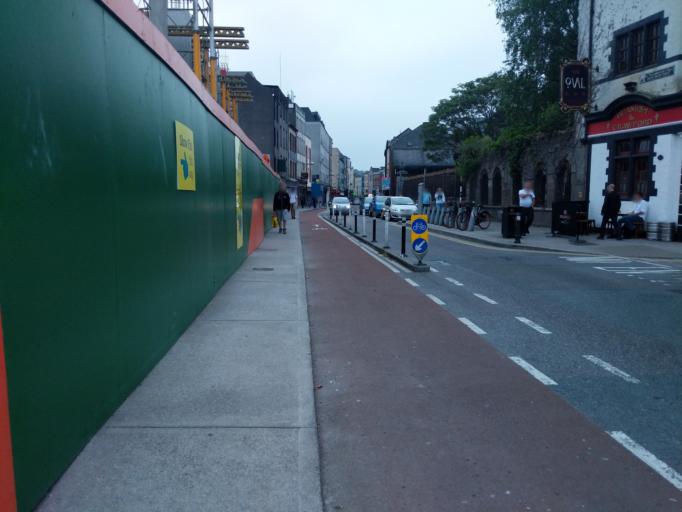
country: IE
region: Munster
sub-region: County Cork
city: Cork
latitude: 51.8966
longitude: -8.4768
